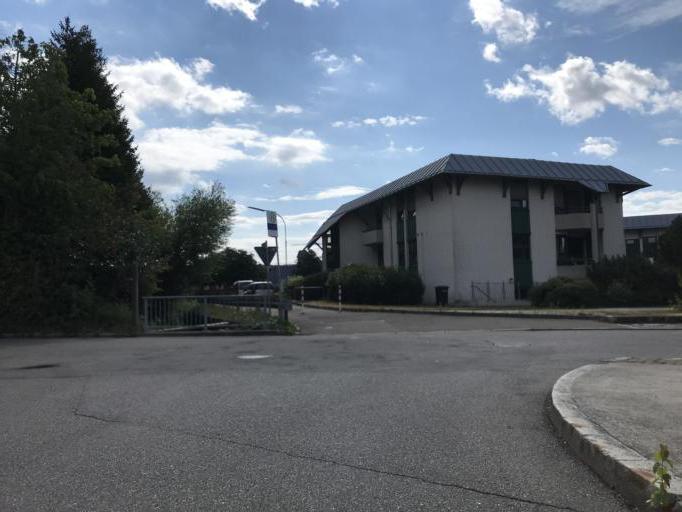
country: DE
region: Baden-Wuerttemberg
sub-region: Freiburg Region
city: Schopfheim
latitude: 47.6449
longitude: 7.8111
